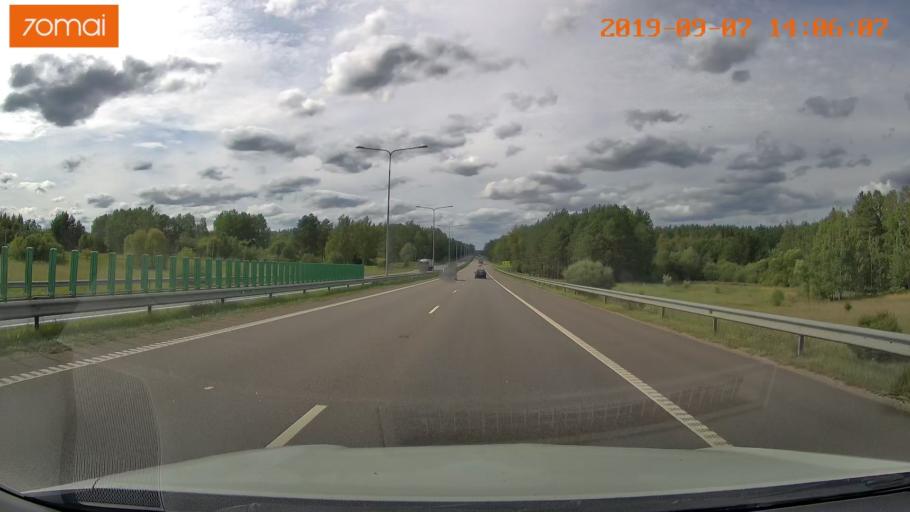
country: LT
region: Vilnius County
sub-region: Vilniaus Rajonas
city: Vievis
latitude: 54.7564
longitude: 24.8945
